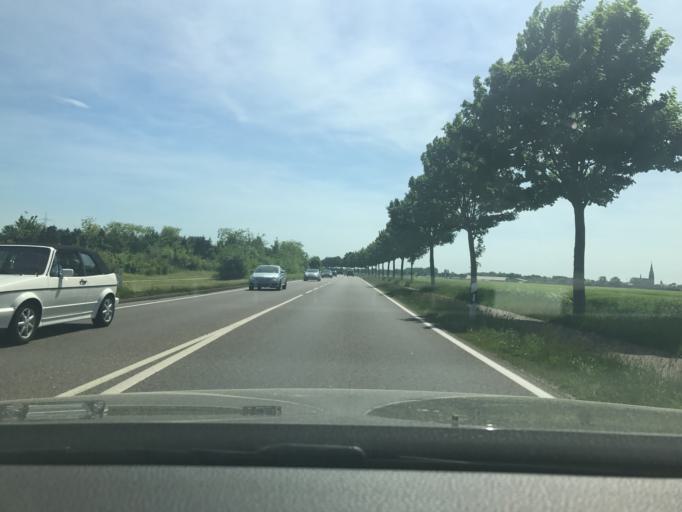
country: DE
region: North Rhine-Westphalia
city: Tonisvorst
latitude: 51.2904
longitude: 6.4775
